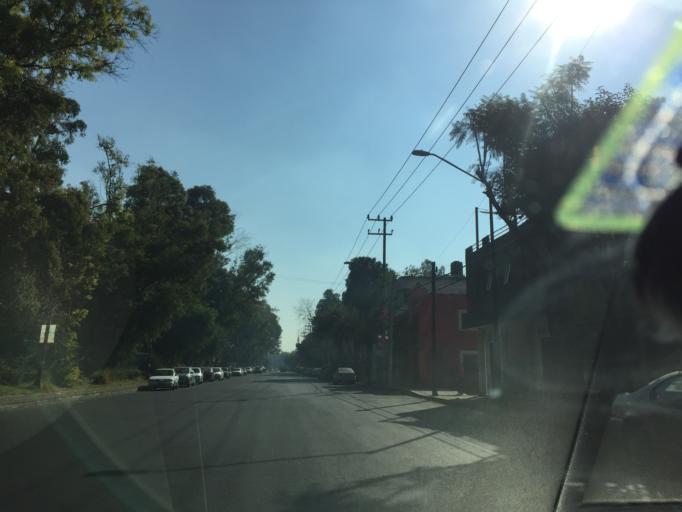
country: MX
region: Mexico
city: Vista Hermosa
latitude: 19.4979
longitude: -99.2116
